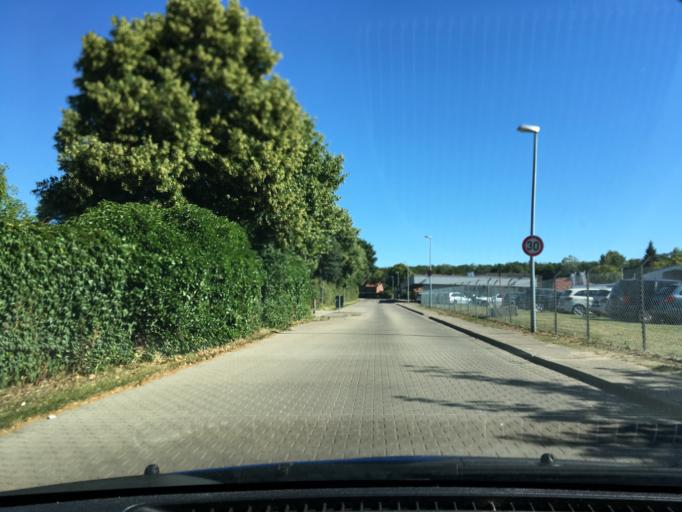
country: DE
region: Lower Saxony
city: Wendisch Evern
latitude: 53.2411
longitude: 10.4521
